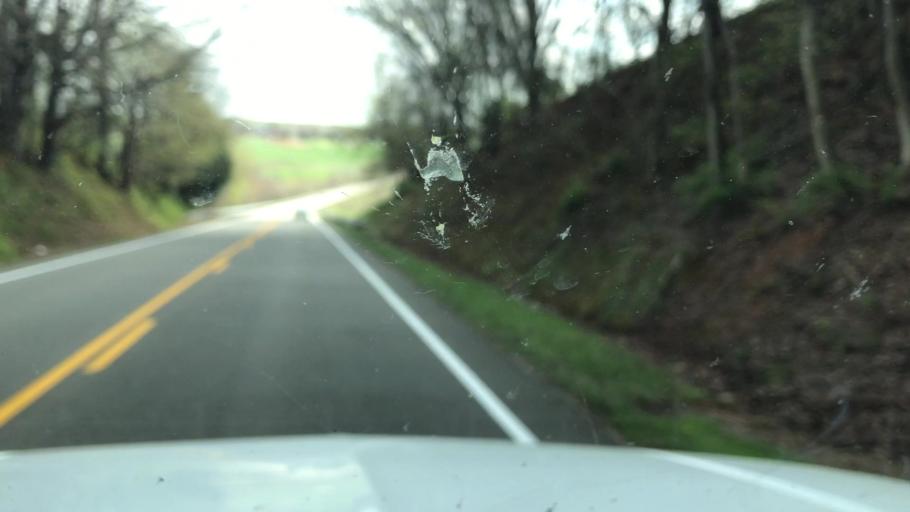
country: US
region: Virginia
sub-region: Goochland County
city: Goochland
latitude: 37.6483
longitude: -77.8326
